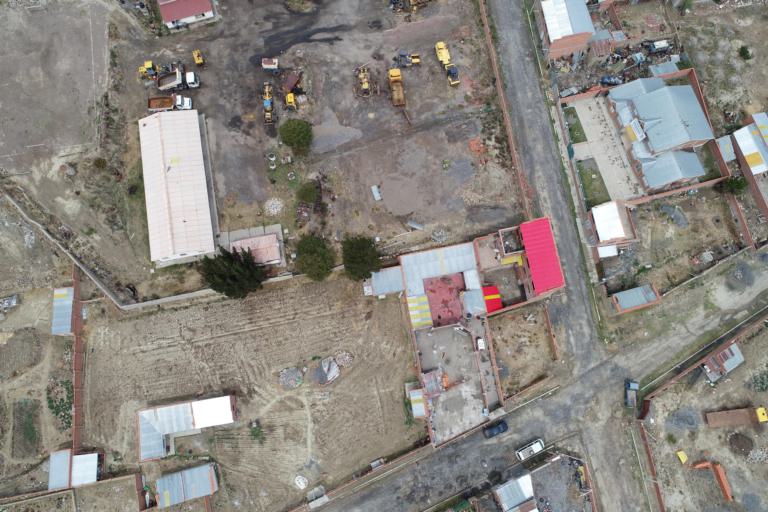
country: BO
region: La Paz
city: Achacachi
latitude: -16.0531
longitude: -68.6823
